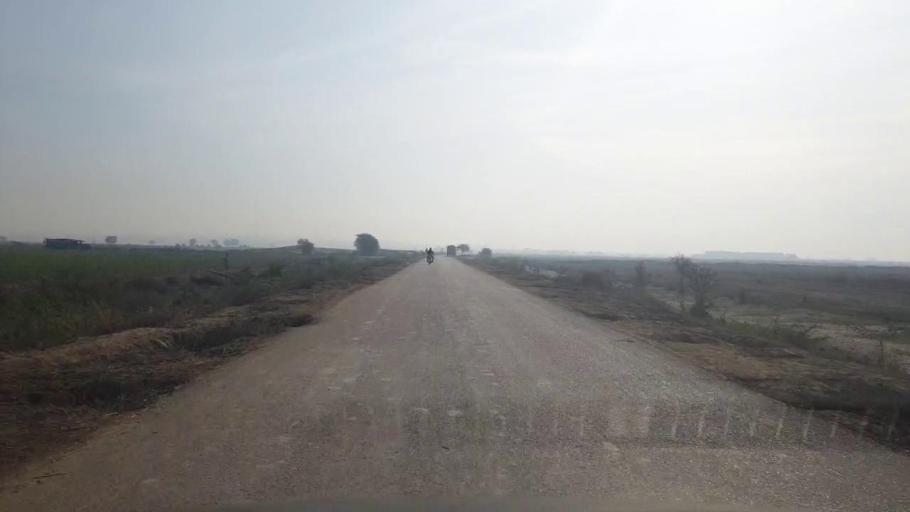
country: PK
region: Sindh
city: Umarkot
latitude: 25.3445
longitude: 69.7075
